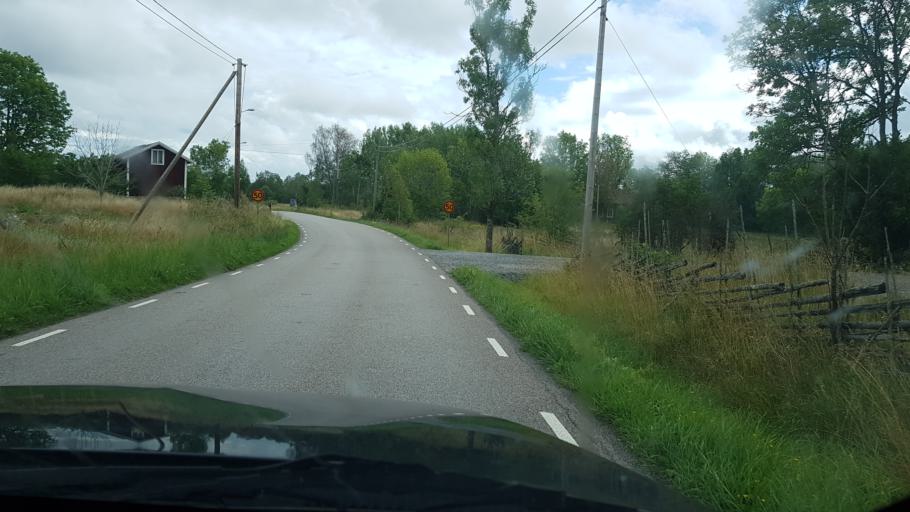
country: SE
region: Uppsala
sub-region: Osthammars Kommun
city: Oregrund
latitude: 60.3565
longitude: 18.4504
